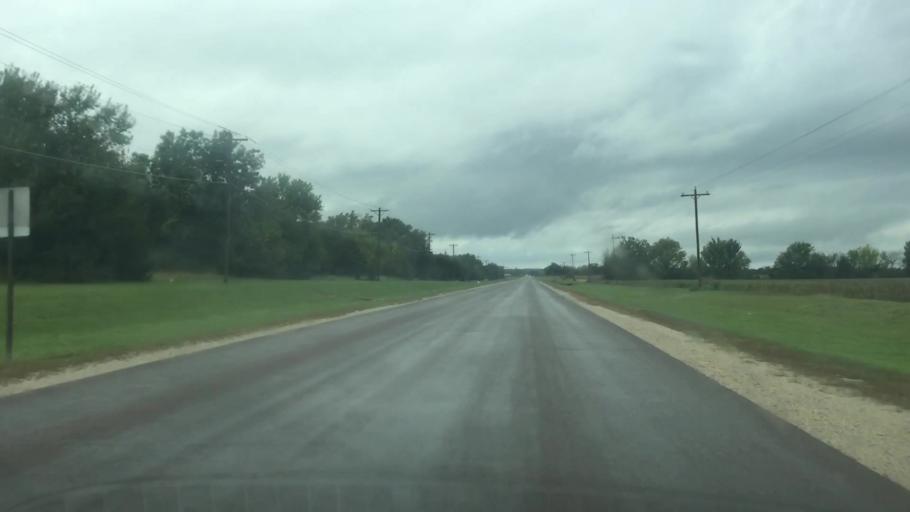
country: US
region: Kansas
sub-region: Allen County
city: Iola
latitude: 37.9513
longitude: -95.3926
